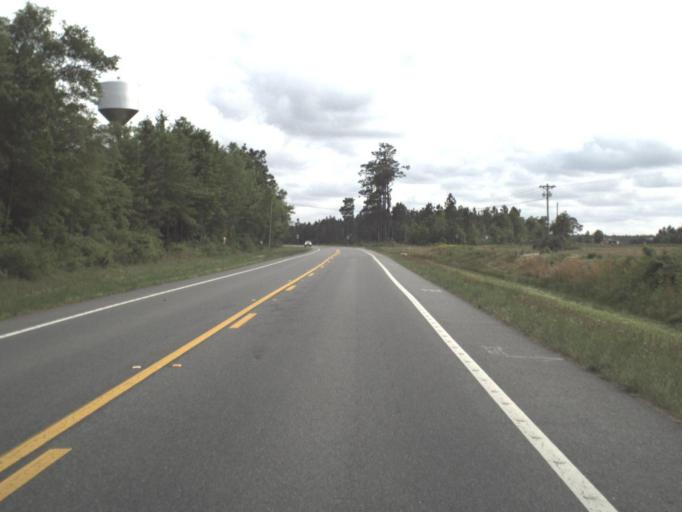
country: US
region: Alabama
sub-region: Escambia County
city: East Brewton
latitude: 30.9739
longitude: -87.0462
